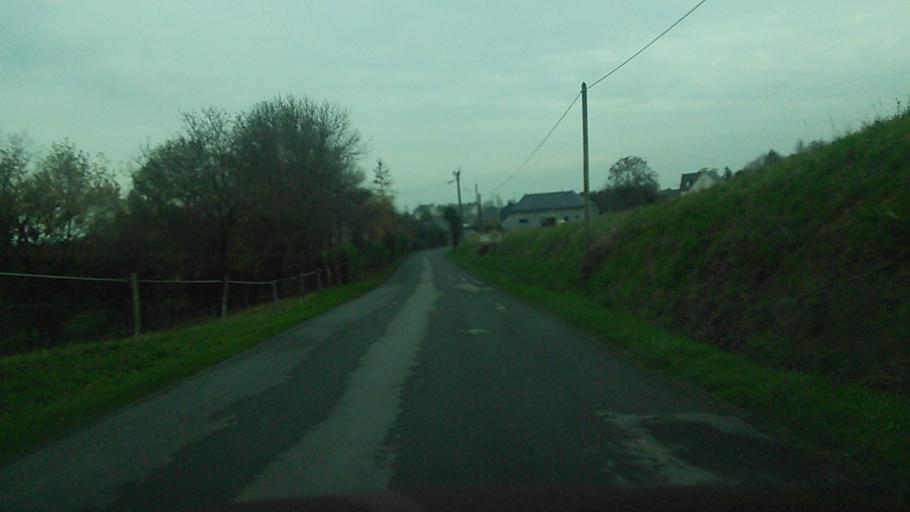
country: FR
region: Brittany
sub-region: Departement des Cotes-d'Armor
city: Yffiniac
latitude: 48.4753
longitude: -2.6557
